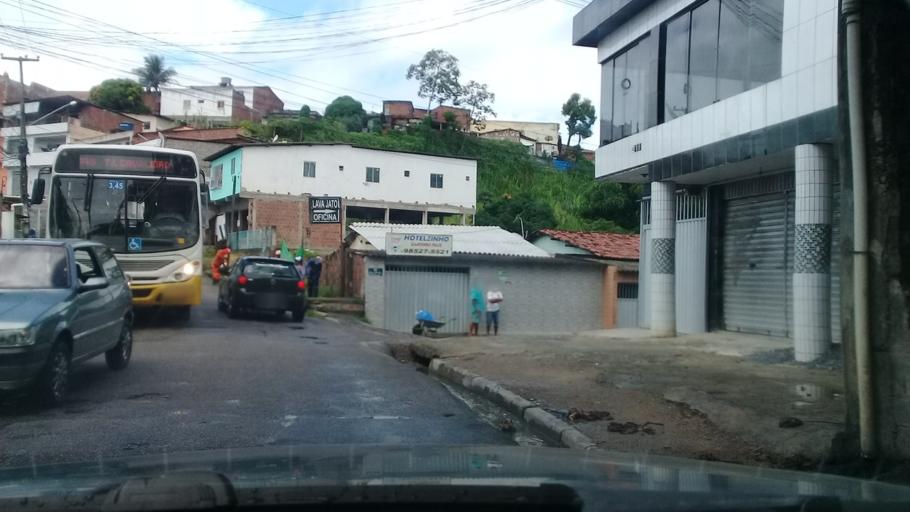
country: BR
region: Pernambuco
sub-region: Jaboatao Dos Guararapes
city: Jaboatao dos Guararapes
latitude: -8.1080
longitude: -34.9629
